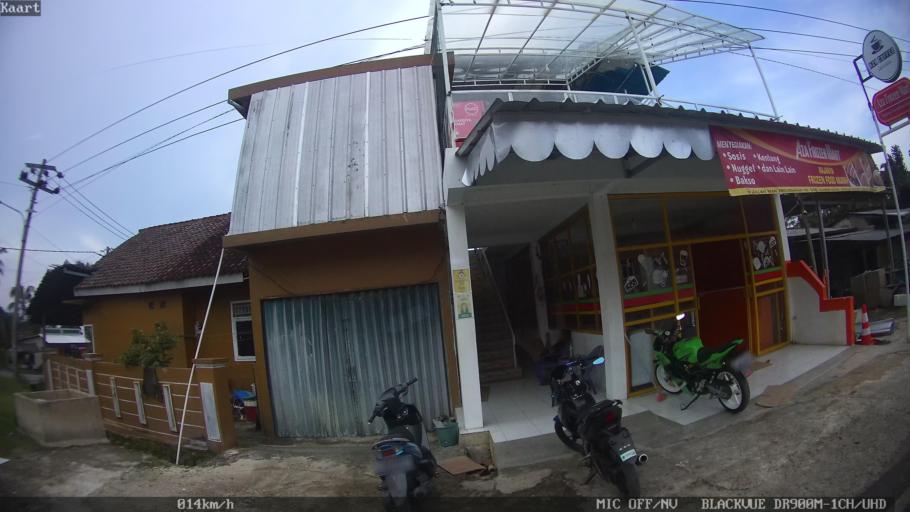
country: ID
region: Lampung
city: Bandarlampung
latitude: -5.4160
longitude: 105.1867
